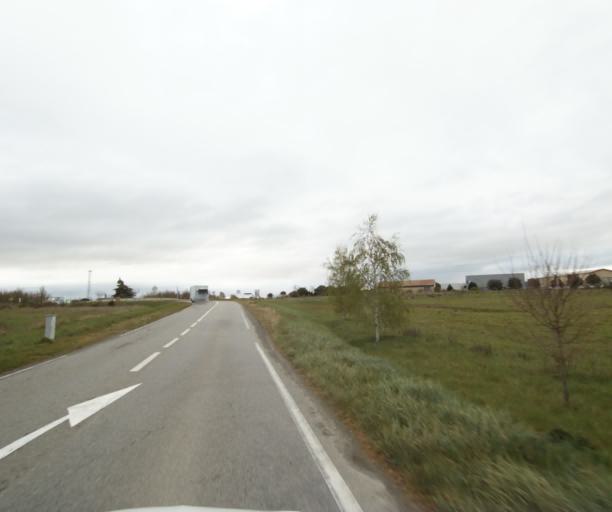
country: FR
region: Midi-Pyrenees
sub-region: Departement de l'Ariege
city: Mazeres
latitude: 43.2326
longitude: 1.6318
